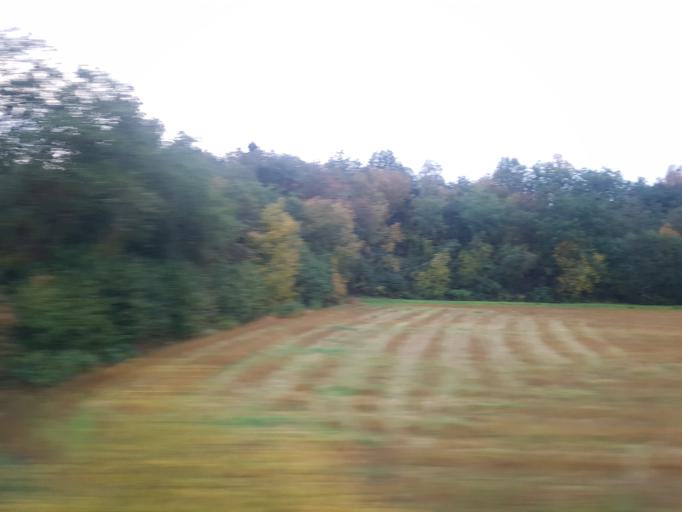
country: NO
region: Sor-Trondelag
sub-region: Melhus
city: Lundamo
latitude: 63.1510
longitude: 10.2821
